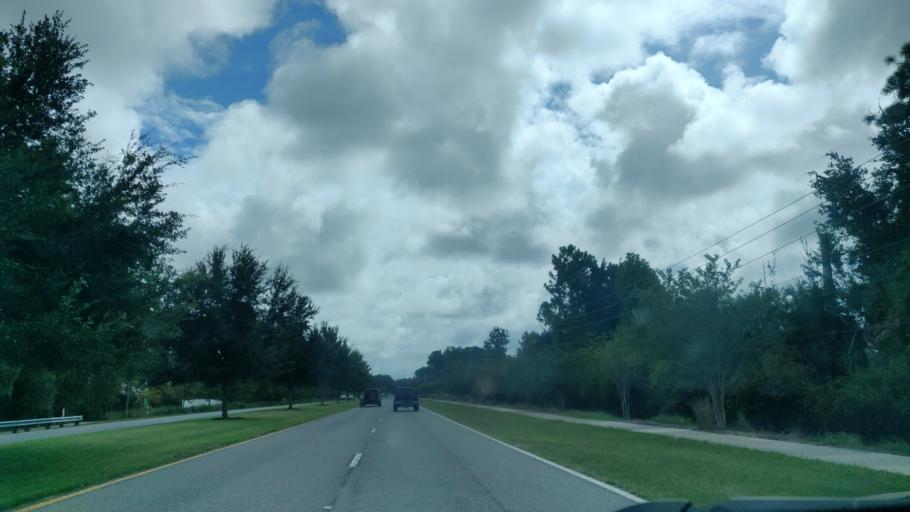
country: US
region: Florida
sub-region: Flagler County
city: Bunnell
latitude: 29.5129
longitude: -81.2223
